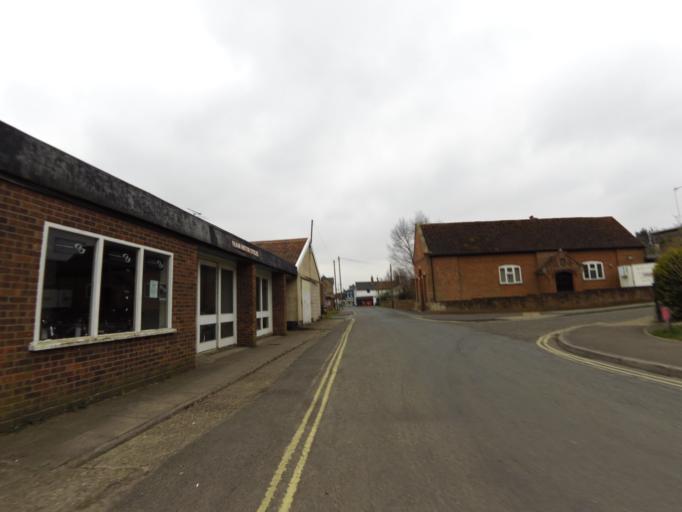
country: GB
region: England
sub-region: Suffolk
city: Framlingham
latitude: 52.2231
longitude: 1.3404
